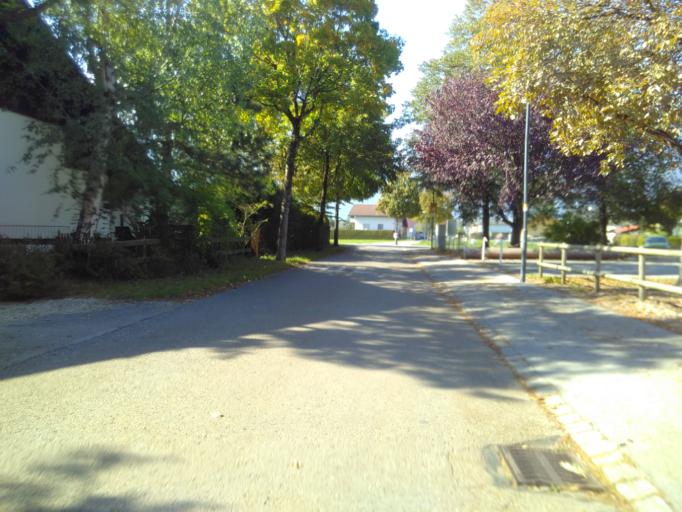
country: AT
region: Vorarlberg
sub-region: Politischer Bezirk Feldkirch
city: Nofels
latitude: 47.2581
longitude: 9.5726
